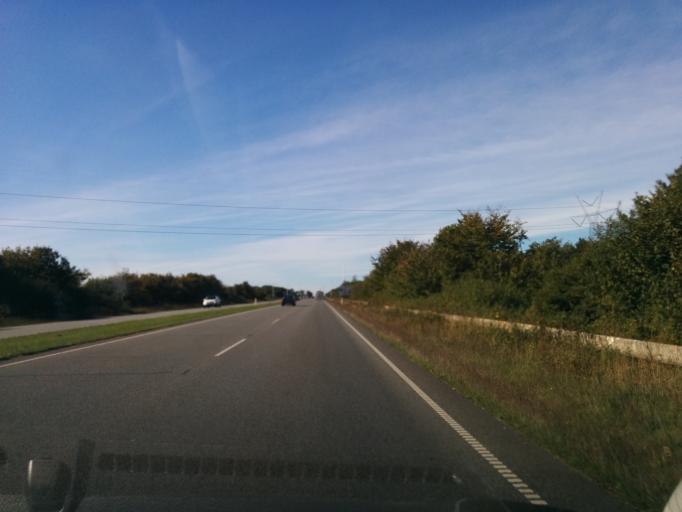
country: DK
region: South Denmark
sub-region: Kolding Kommune
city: Kolding
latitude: 55.4668
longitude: 9.4459
